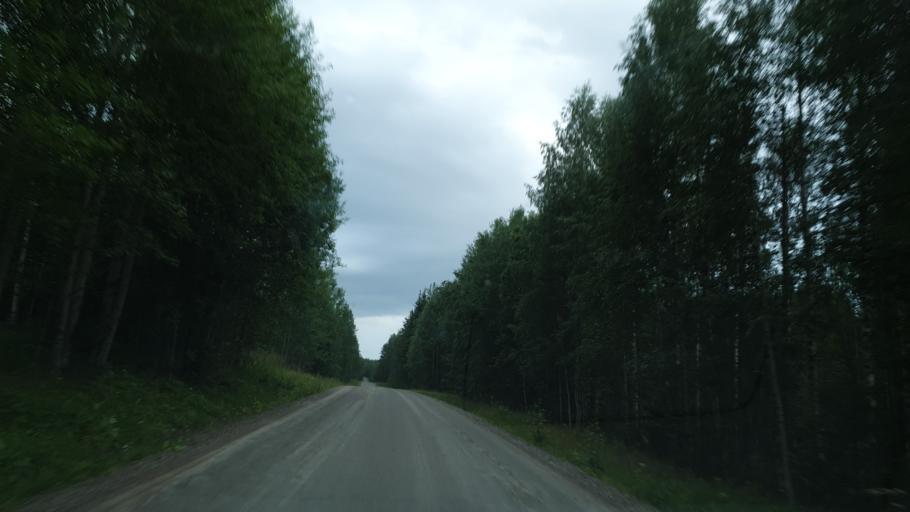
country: FI
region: Kainuu
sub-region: Kehys-Kainuu
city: Kuhmo
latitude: 64.1957
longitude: 29.3674
